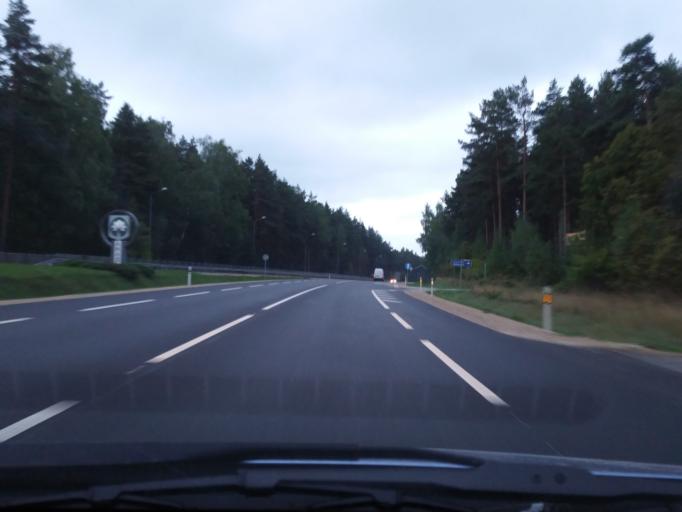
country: LV
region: Adazi
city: Adazi
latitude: 57.0600
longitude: 24.3220
